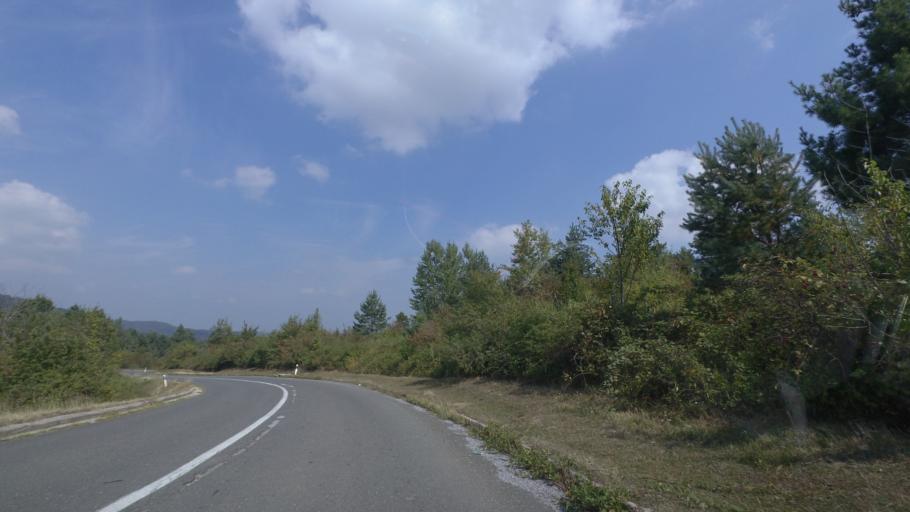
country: BA
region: Federation of Bosnia and Herzegovina
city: Zboriste
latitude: 45.1630
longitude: 16.1389
